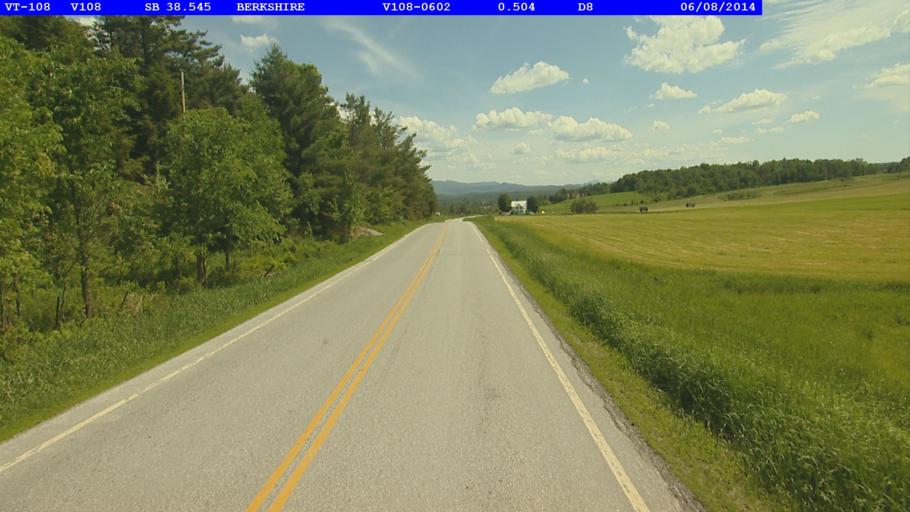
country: US
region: Vermont
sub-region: Franklin County
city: Enosburg Falls
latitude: 44.9320
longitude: -72.8119
